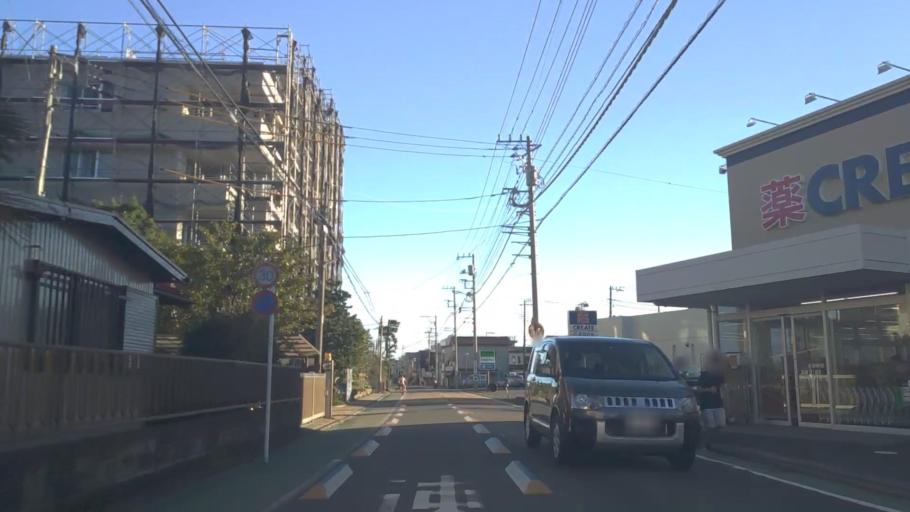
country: JP
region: Kanagawa
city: Chigasaki
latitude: 35.3303
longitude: 139.4145
